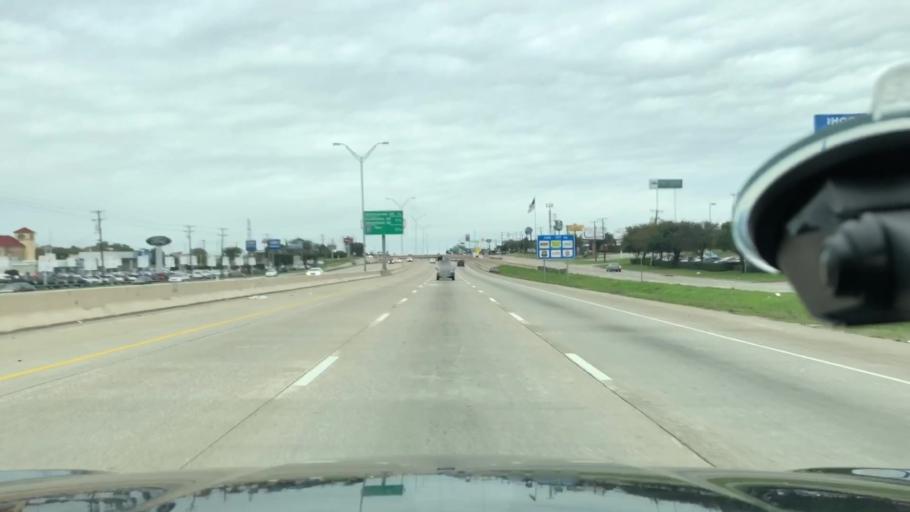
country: US
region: Texas
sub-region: Dallas County
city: DeSoto
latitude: 32.5968
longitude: -96.8224
